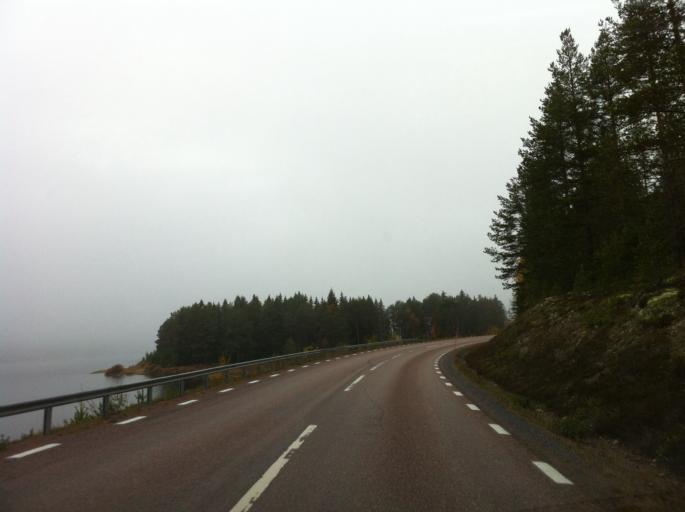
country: NO
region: Hedmark
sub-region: Trysil
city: Innbygda
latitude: 61.8513
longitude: 12.7534
